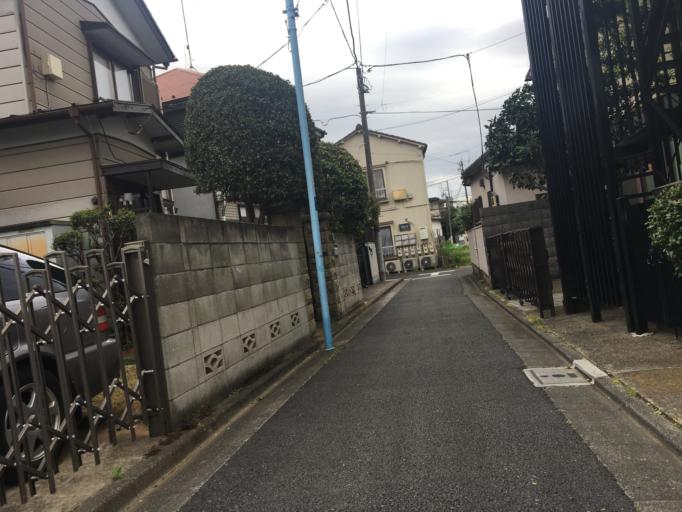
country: JP
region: Tokyo
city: Tokyo
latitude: 35.6961
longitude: 139.6362
